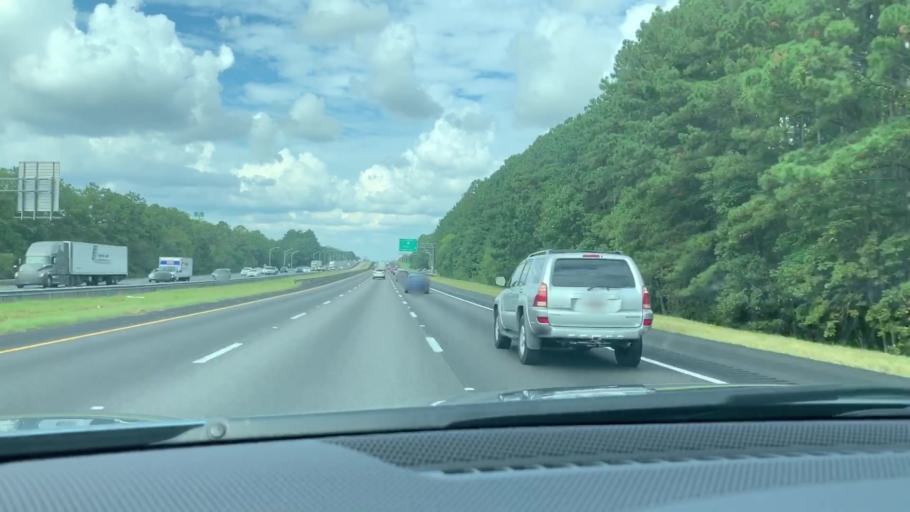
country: US
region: Georgia
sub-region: Chatham County
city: Pooler
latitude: 32.1051
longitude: -81.2371
